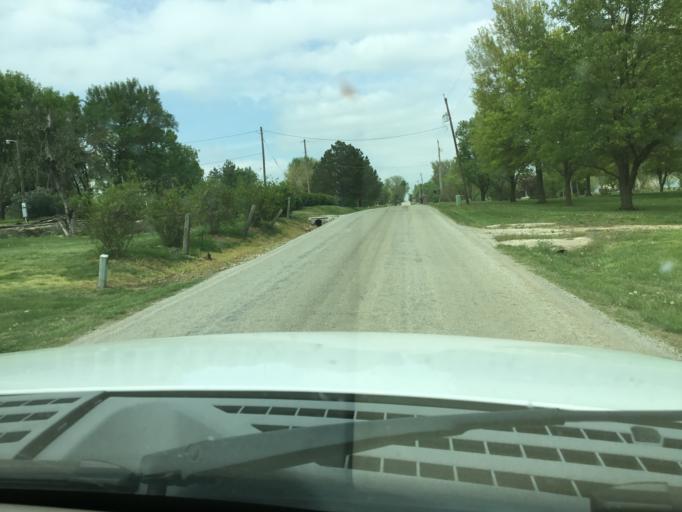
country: US
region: Kansas
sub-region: Shawnee County
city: Topeka
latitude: 38.9756
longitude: -95.5863
